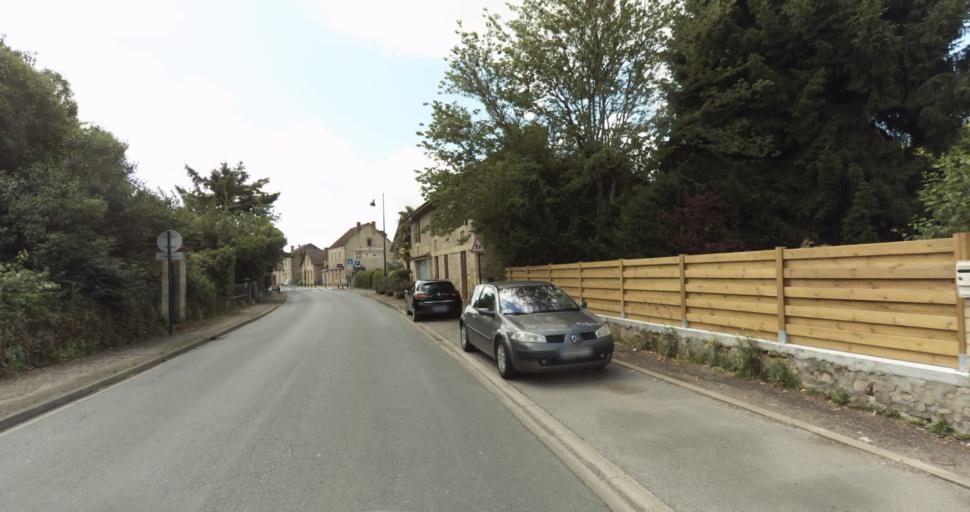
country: FR
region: Aquitaine
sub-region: Departement de la Dordogne
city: Lalinde
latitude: 44.8300
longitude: 0.7038
